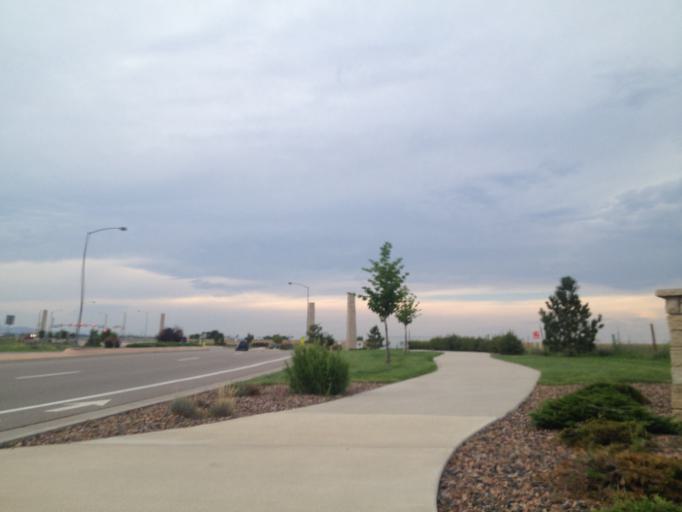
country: US
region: Colorado
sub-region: Boulder County
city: Louisville
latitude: 39.9466
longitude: -105.1233
